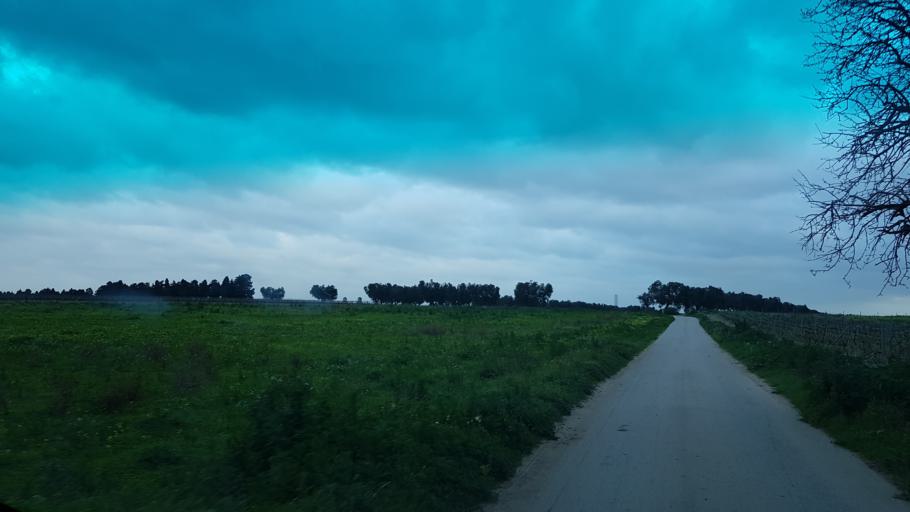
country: IT
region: Apulia
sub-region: Provincia di Brindisi
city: La Rosa
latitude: 40.5937
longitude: 17.9760
